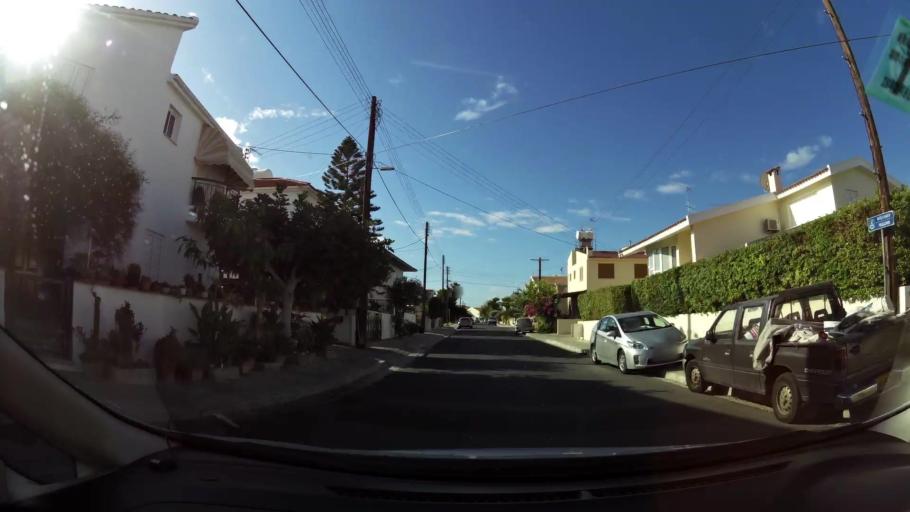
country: CY
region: Lefkosia
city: Nicosia
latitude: 35.1327
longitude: 33.3489
